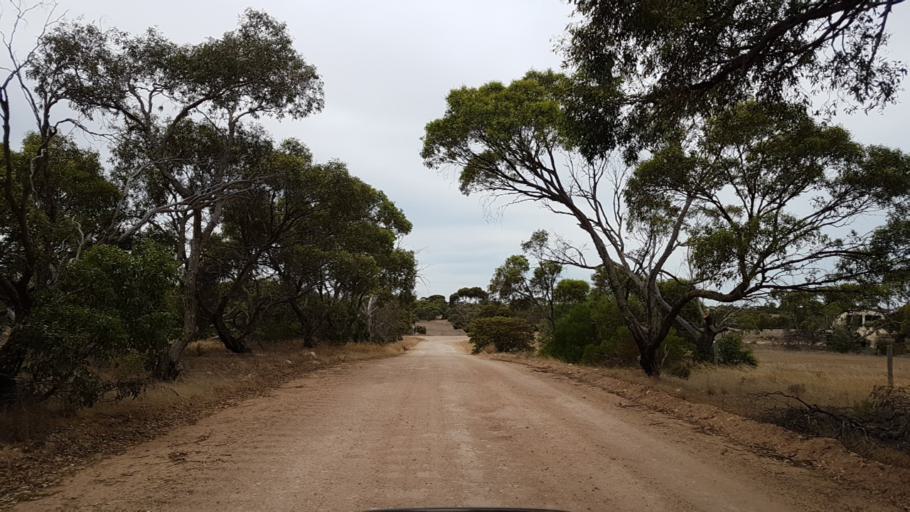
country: AU
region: South Australia
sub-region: Yorke Peninsula
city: Port Victoria
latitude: -34.7776
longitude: 137.6014
